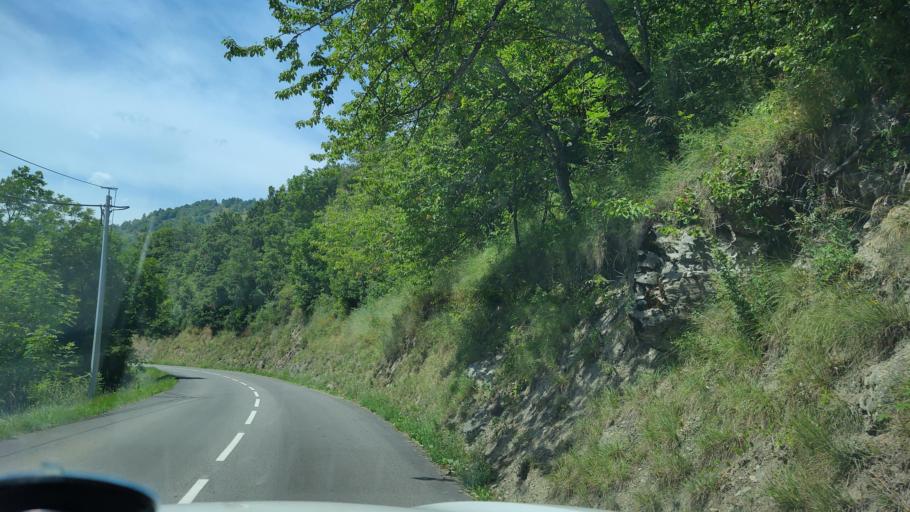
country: FR
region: Rhone-Alpes
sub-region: Departement de la Savoie
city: Les Allues
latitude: 45.4587
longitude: 6.5836
